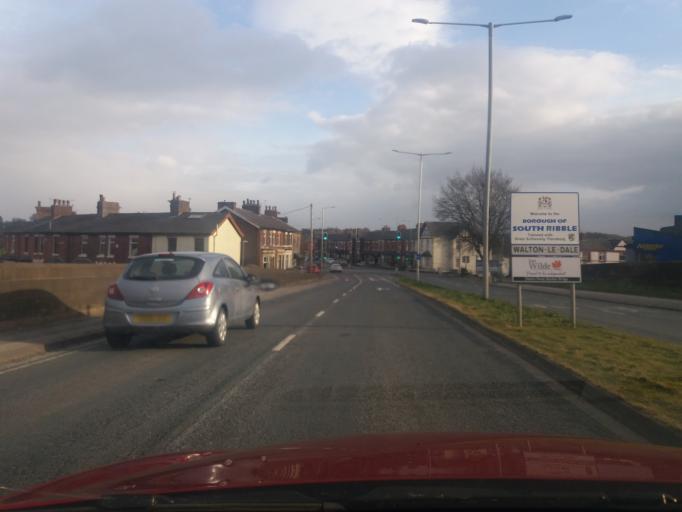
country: GB
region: England
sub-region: Lancashire
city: Preston
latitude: 53.7527
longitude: -2.6793
